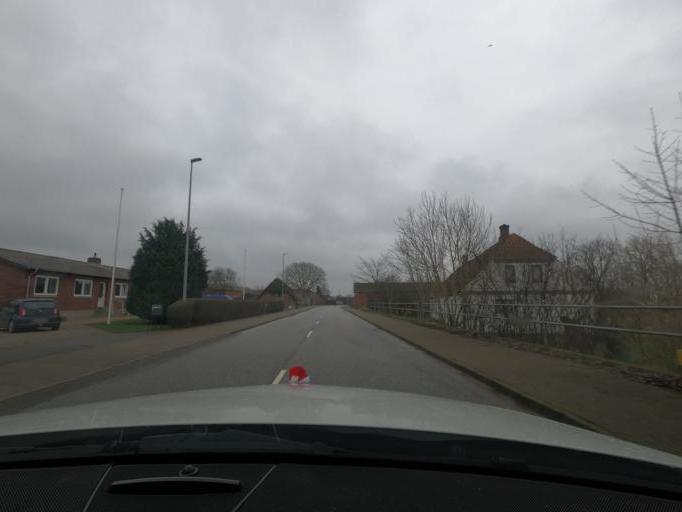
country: DK
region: South Denmark
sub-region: Haderslev Kommune
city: Starup
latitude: 55.2553
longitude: 9.6661
